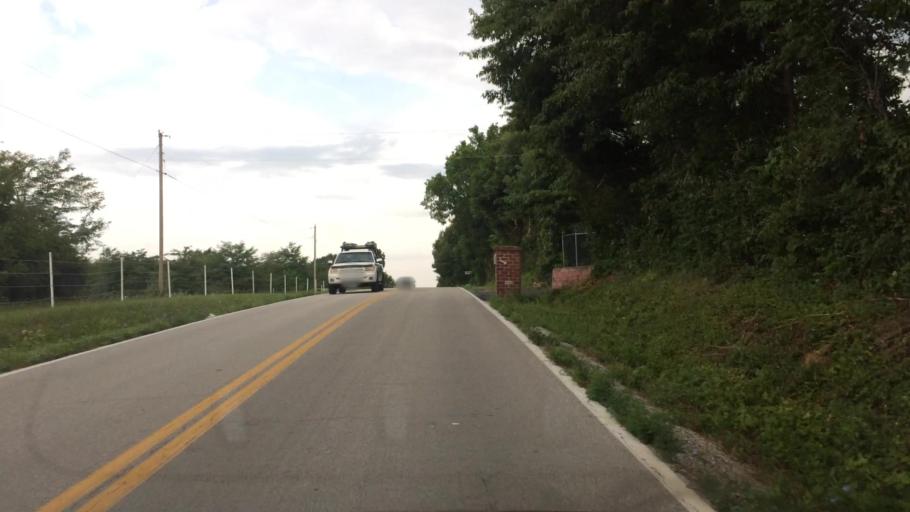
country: US
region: Missouri
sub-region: Greene County
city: Strafford
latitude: 37.2721
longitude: -93.1920
